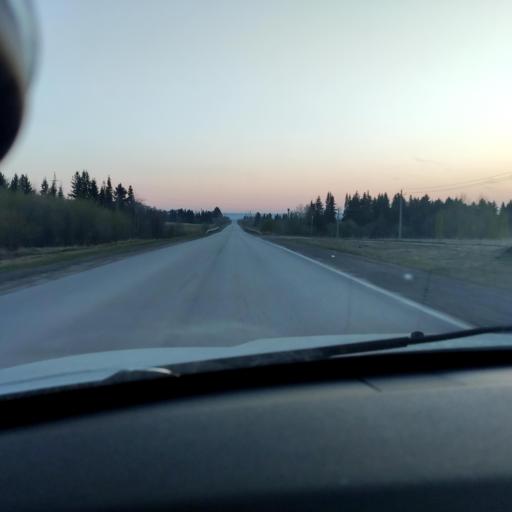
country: RU
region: Perm
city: Lobanovo
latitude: 57.8517
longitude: 56.2960
